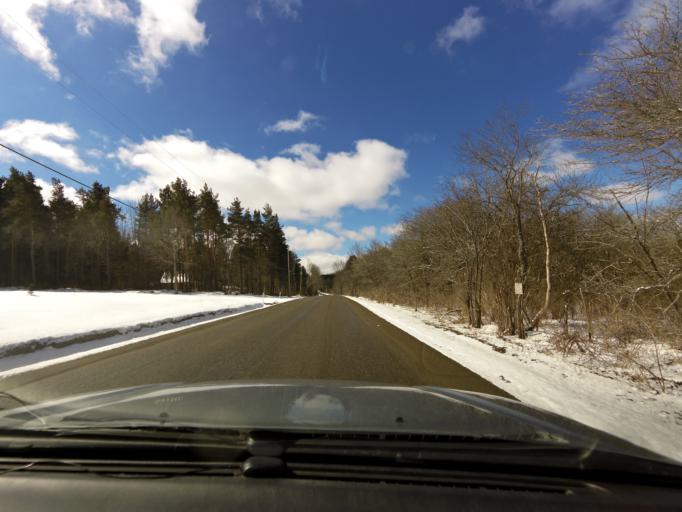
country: US
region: New York
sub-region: Cattaraugus County
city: Franklinville
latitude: 42.3680
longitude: -78.4088
